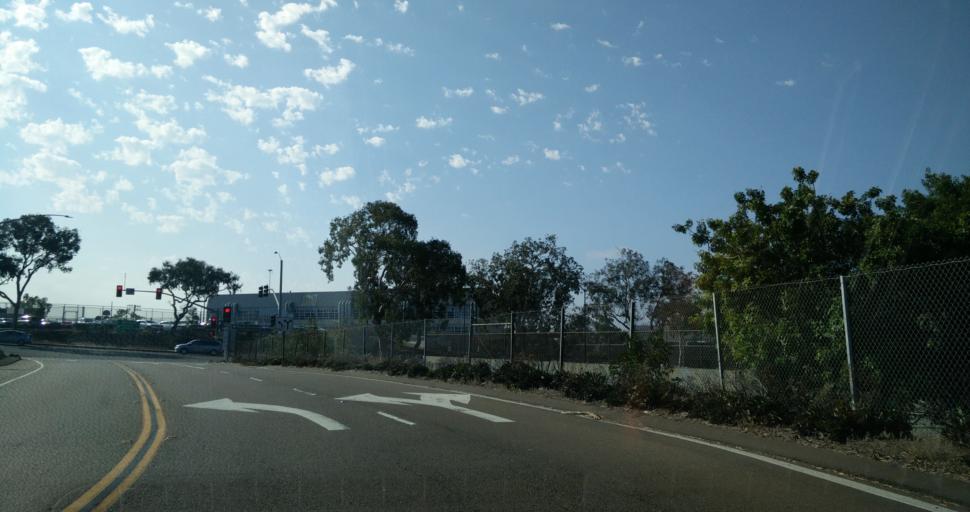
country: US
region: California
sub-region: San Diego County
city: San Diego
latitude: 32.7227
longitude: -117.1532
